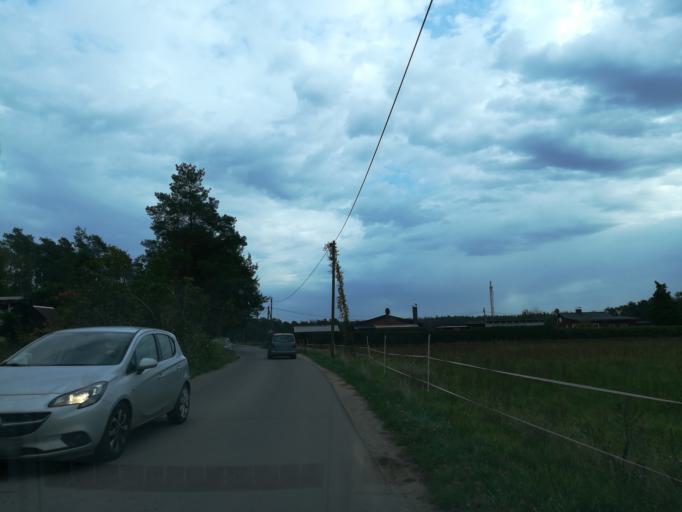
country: DE
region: Saxony-Anhalt
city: Plotzky
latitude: 52.0615
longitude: 11.8017
